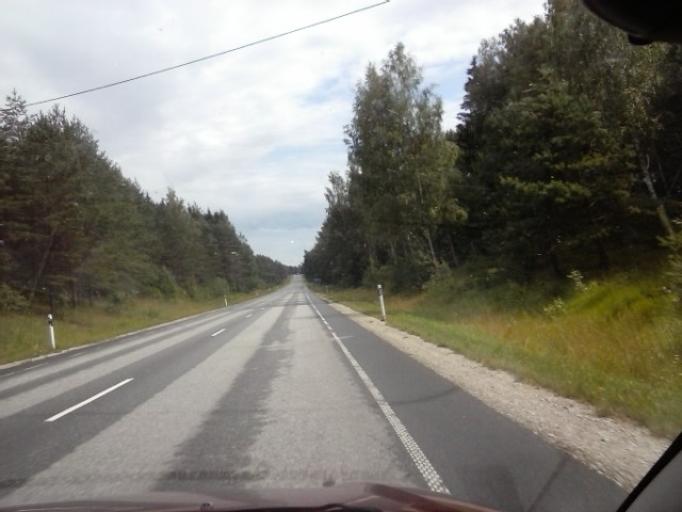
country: EE
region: Tartu
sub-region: UElenurme vald
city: Ulenurme
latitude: 58.3478
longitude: 26.9376
